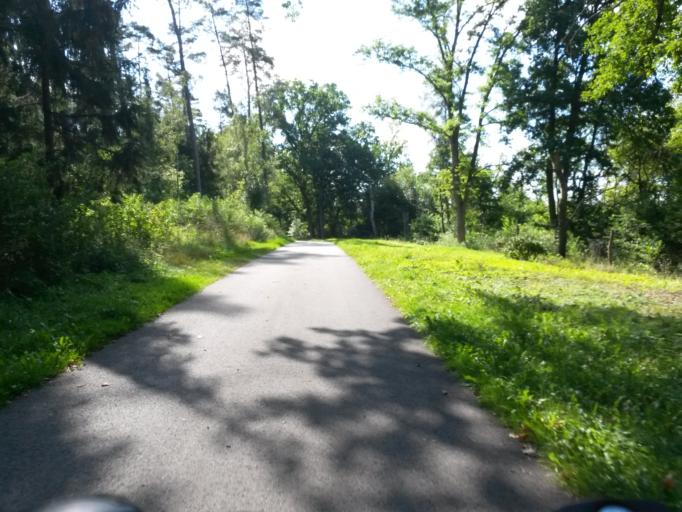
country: DE
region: Brandenburg
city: Lychen
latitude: 53.1647
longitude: 13.3995
